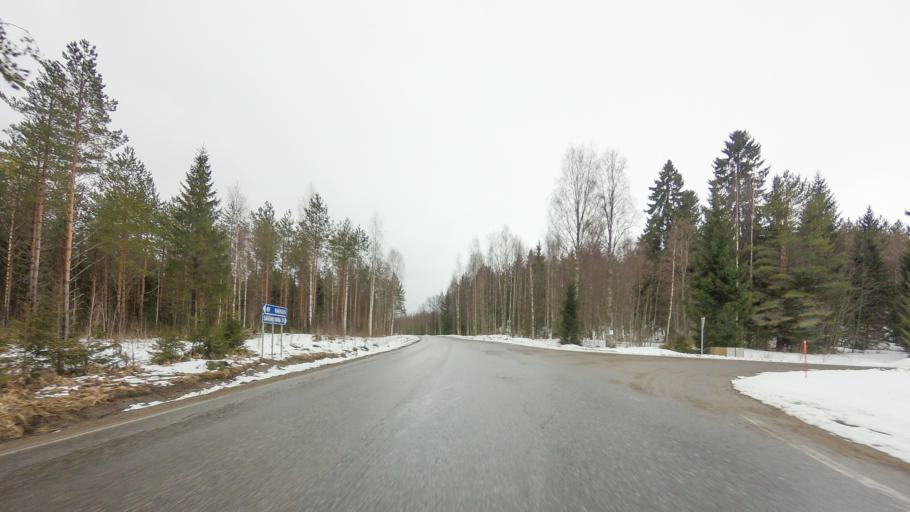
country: FI
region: Southern Savonia
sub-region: Savonlinna
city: Savonlinna
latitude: 61.9206
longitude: 28.8961
